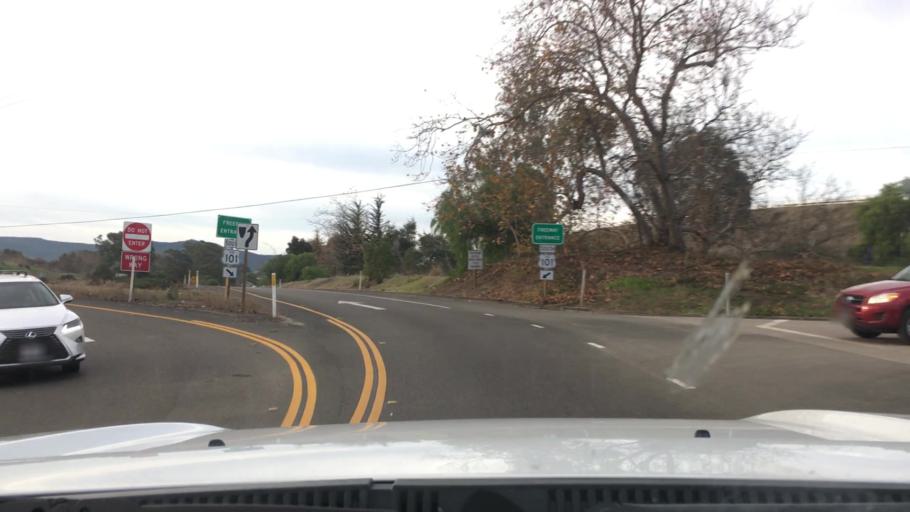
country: US
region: California
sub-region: San Luis Obispo County
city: San Luis Obispo
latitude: 35.2739
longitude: -120.6723
